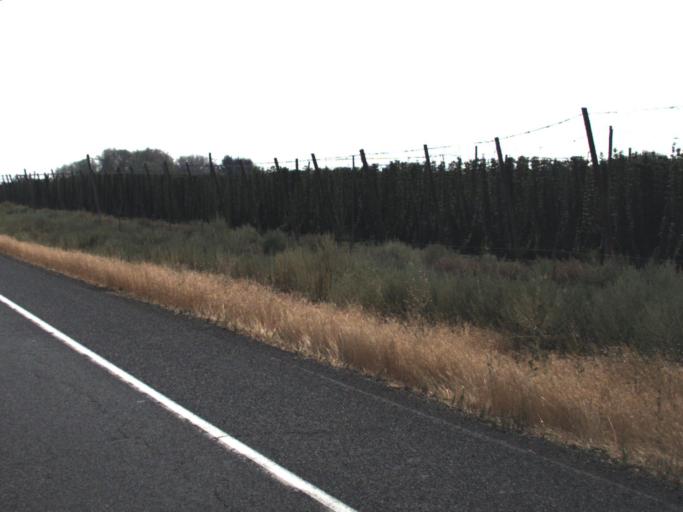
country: US
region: Washington
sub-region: Yakima County
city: Zillah
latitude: 46.5287
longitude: -120.2663
